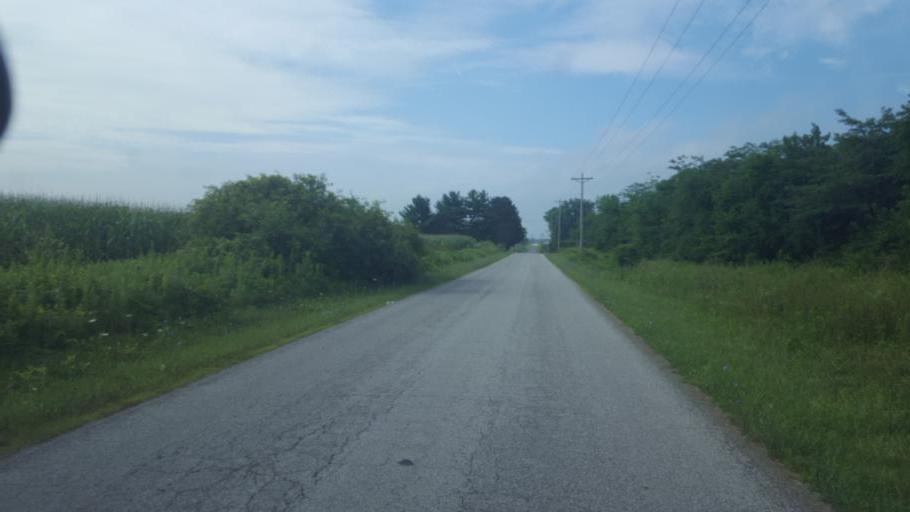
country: US
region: Ohio
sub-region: Delaware County
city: Ashley
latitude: 40.3953
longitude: -82.9115
